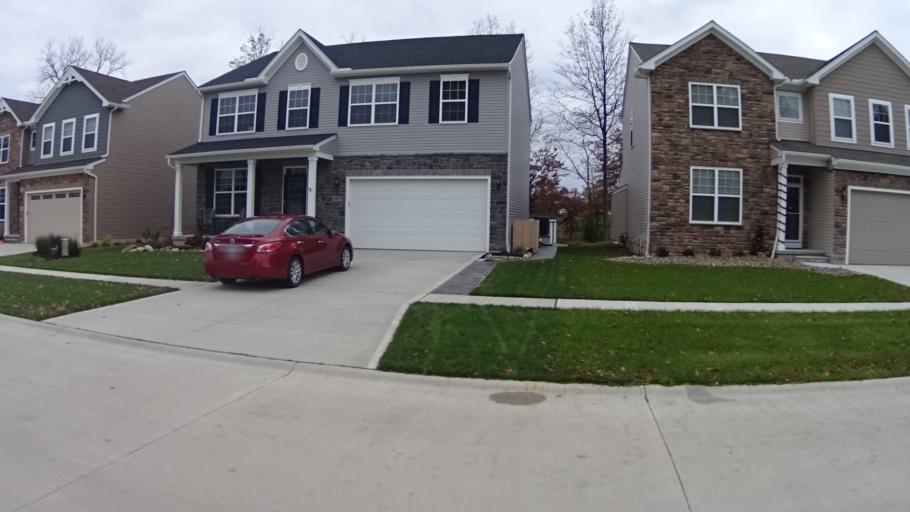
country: US
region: Ohio
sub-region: Lorain County
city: Avon Lake
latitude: 41.4850
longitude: -82.0221
